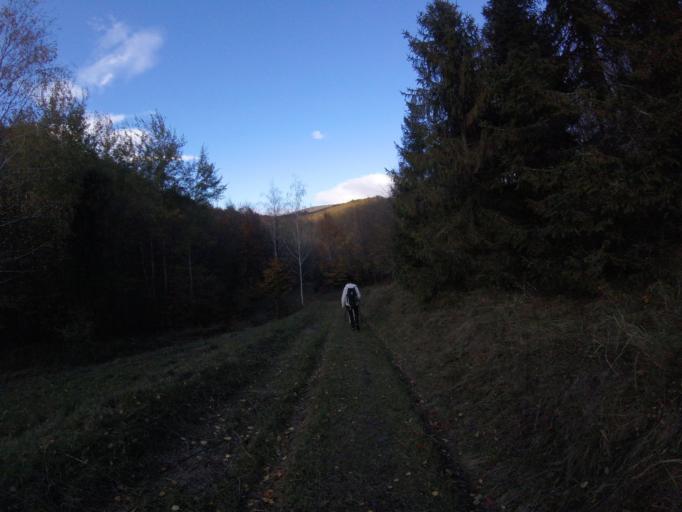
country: HU
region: Borsod-Abauj-Zemplen
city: Tolcsva
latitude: 48.3765
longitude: 21.3802
